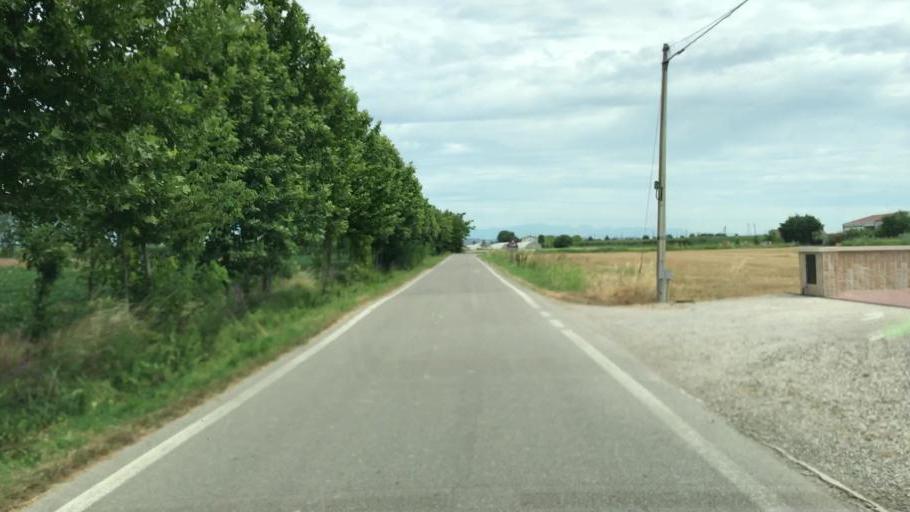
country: IT
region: Lombardy
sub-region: Provincia di Mantova
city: Ceresara
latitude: 45.2659
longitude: 10.5905
